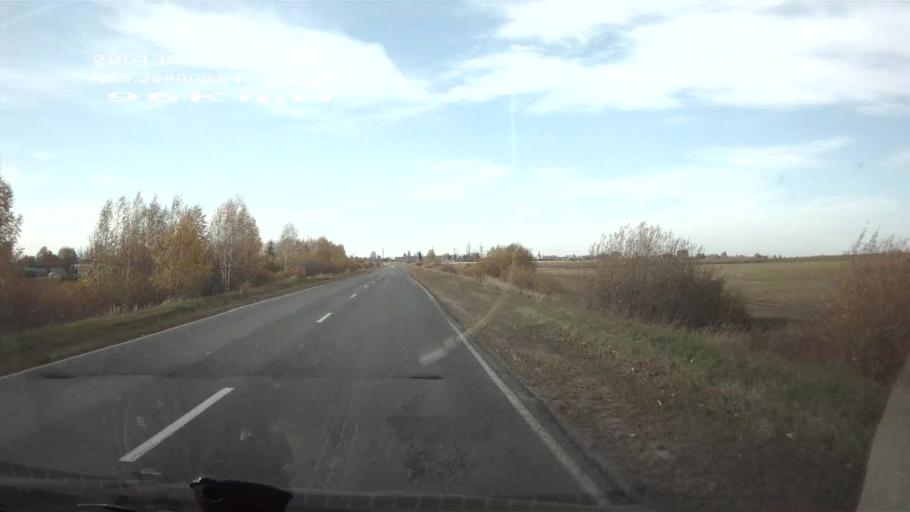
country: RU
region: Chuvashia
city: Ibresi
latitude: 55.2890
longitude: 47.0676
